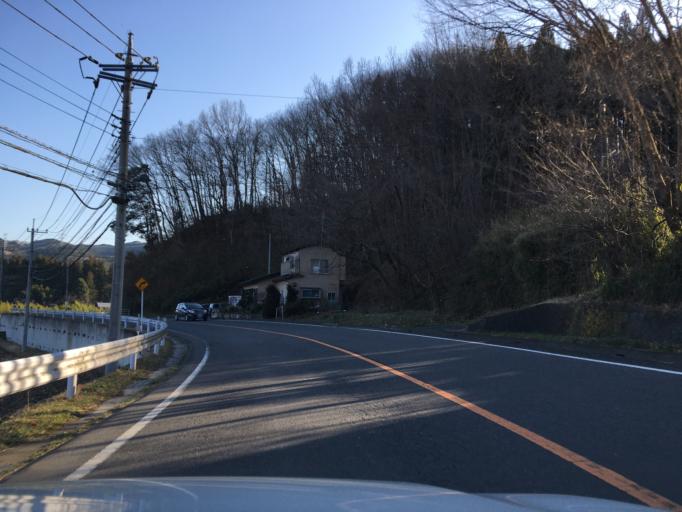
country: JP
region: Ibaraki
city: Daigo
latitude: 36.7806
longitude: 140.3060
